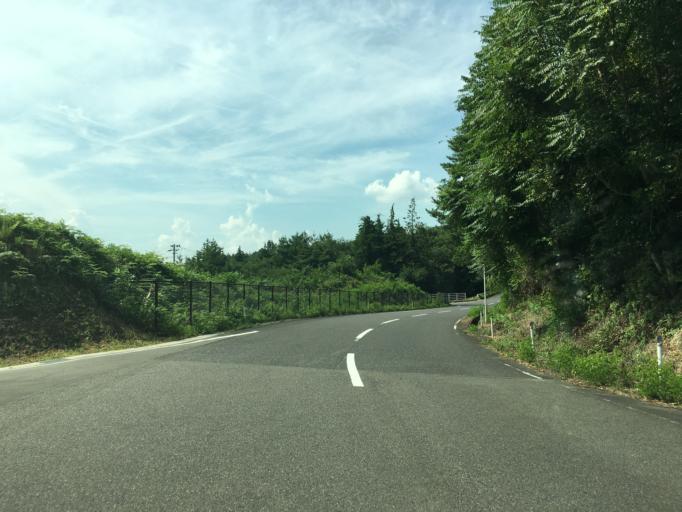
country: JP
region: Fukushima
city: Sukagawa
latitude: 37.2233
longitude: 140.4219
